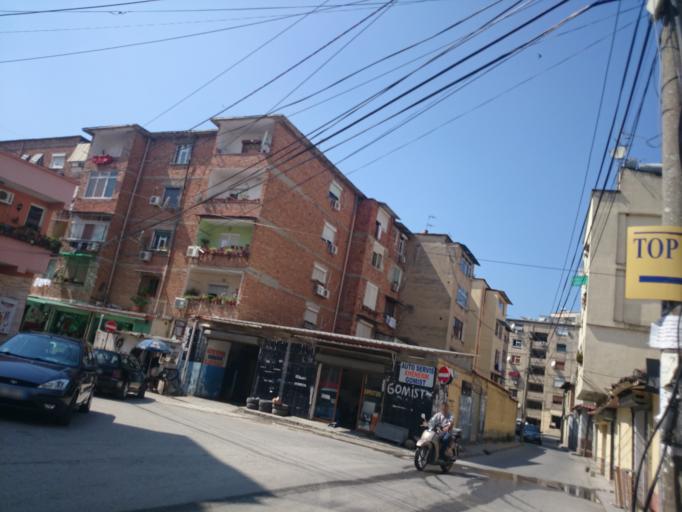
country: AL
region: Tirane
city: Tirana
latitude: 41.3268
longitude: 19.8311
